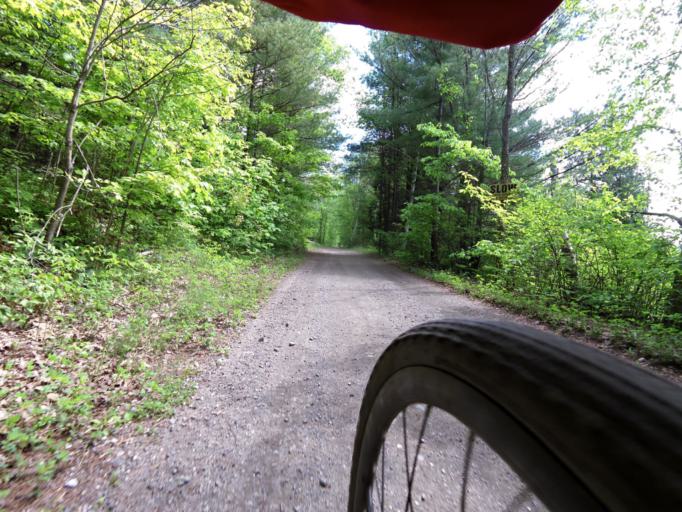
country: CA
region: Ontario
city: Renfrew
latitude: 45.2011
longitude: -76.6857
